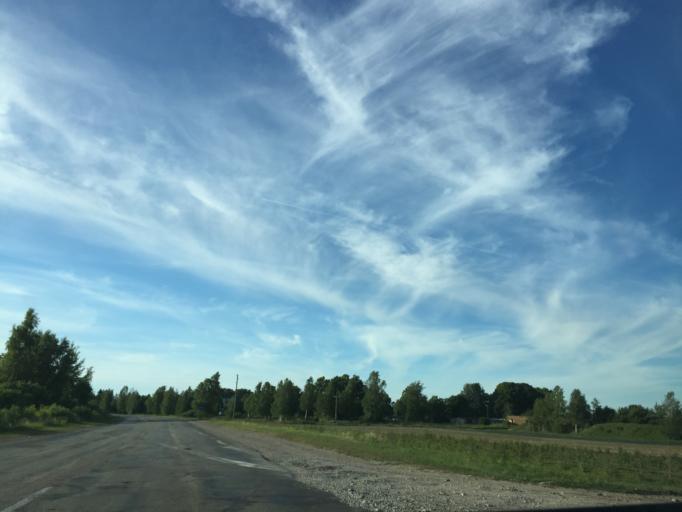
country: LV
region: Ventspils
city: Ventspils
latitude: 57.3006
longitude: 21.5617
